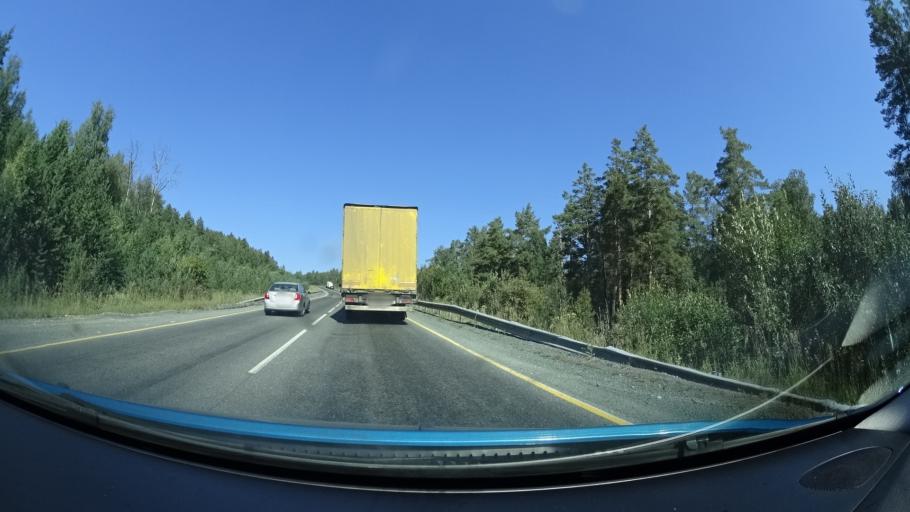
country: RU
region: Bashkortostan
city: Abzakovo
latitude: 53.8868
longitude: 58.5271
